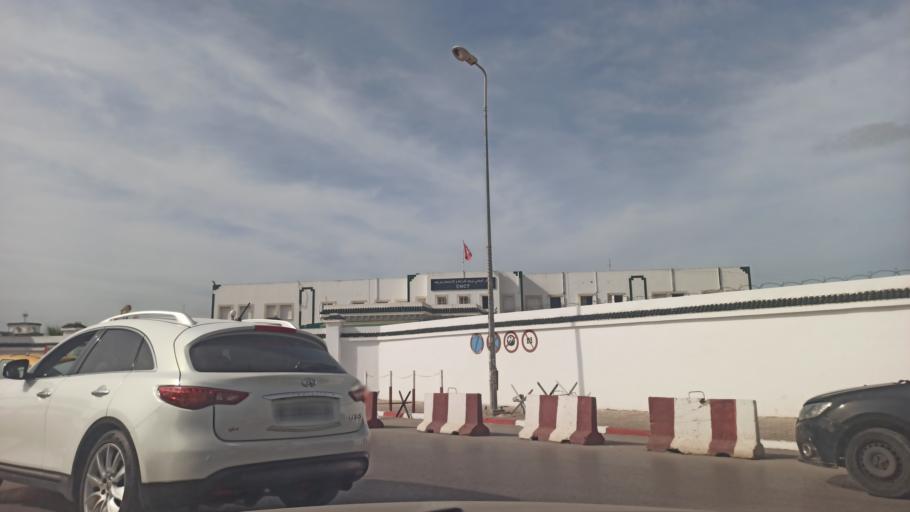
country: TN
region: Tunis
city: La Goulette
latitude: 36.8495
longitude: 10.2594
